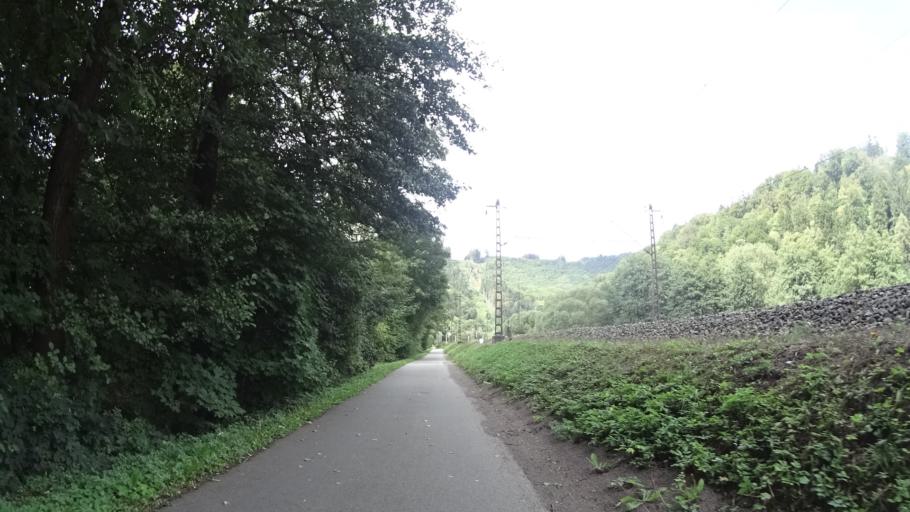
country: CZ
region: Pardubicky
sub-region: Okres Usti nad Orlici
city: Usti nad Orlici
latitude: 49.9739
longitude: 16.3438
